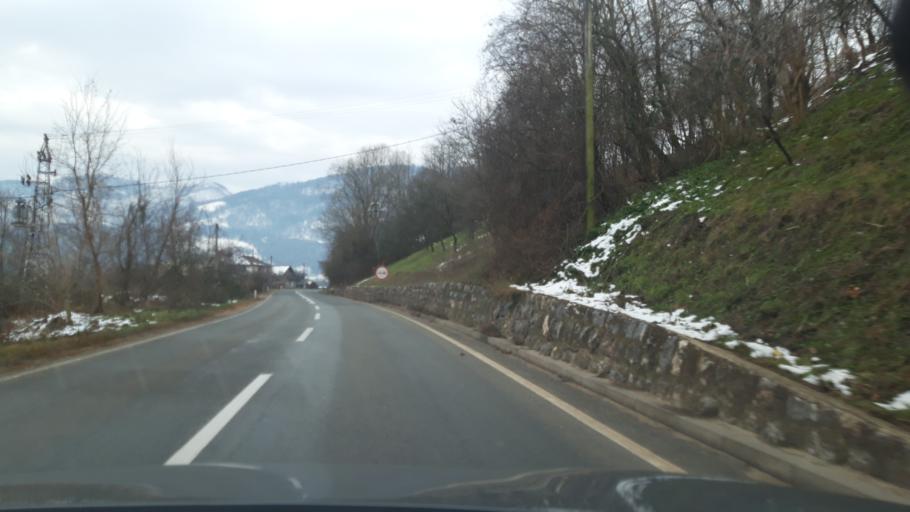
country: RS
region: Central Serbia
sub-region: Macvanski Okrug
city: Mali Zvornik
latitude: 44.2947
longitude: 19.1493
